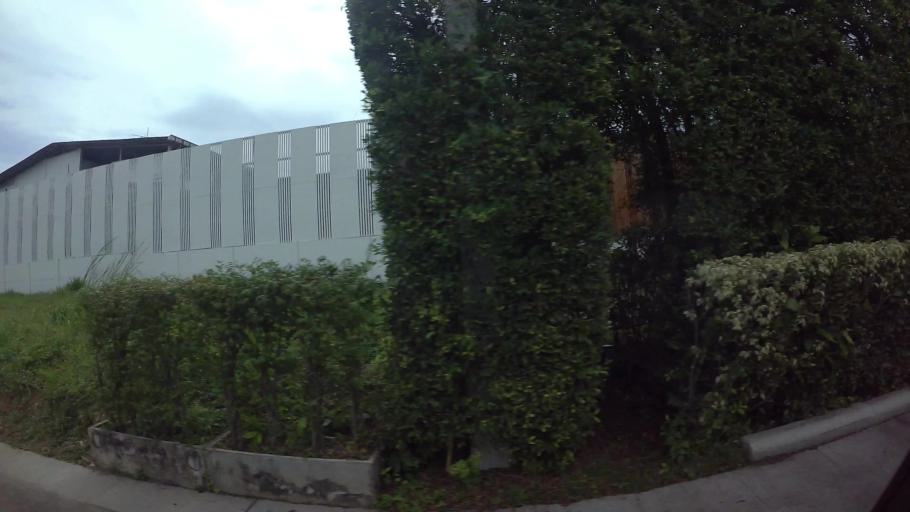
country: TH
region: Chon Buri
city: Si Racha
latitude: 13.1568
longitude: 100.9788
